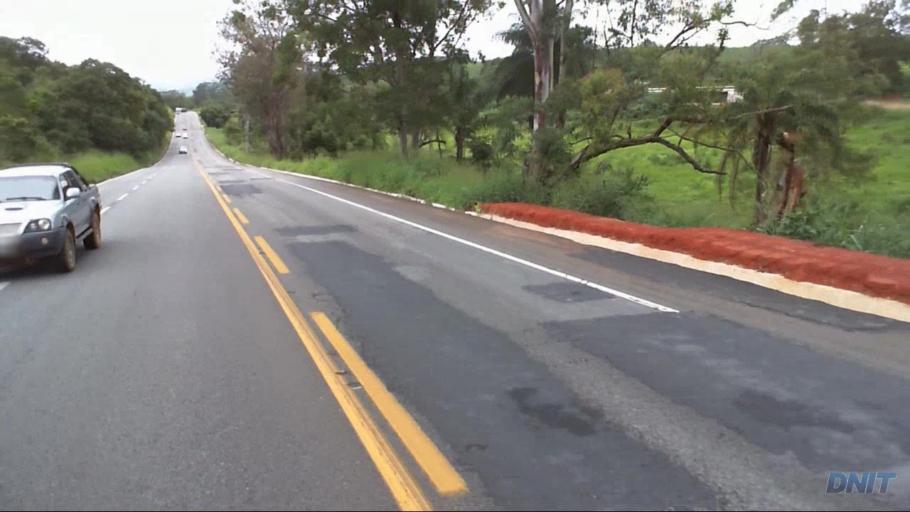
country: BR
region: Minas Gerais
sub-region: Joao Monlevade
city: Joao Monlevade
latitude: -19.8510
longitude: -43.2979
